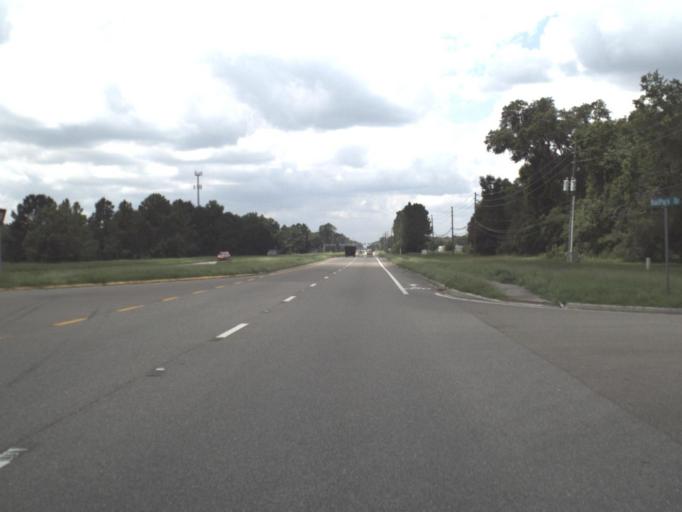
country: US
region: Florida
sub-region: Hernando County
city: Masaryktown
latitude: 28.4677
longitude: -82.4432
